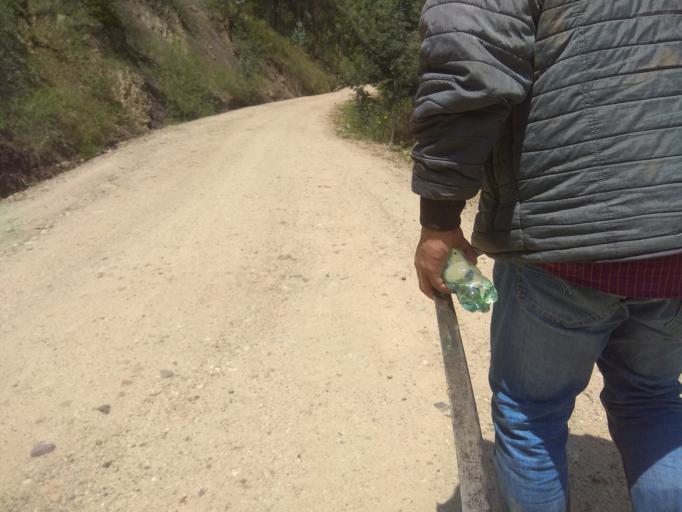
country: CO
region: Boyaca
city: Socha Viejo
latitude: 5.9781
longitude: -72.7284
